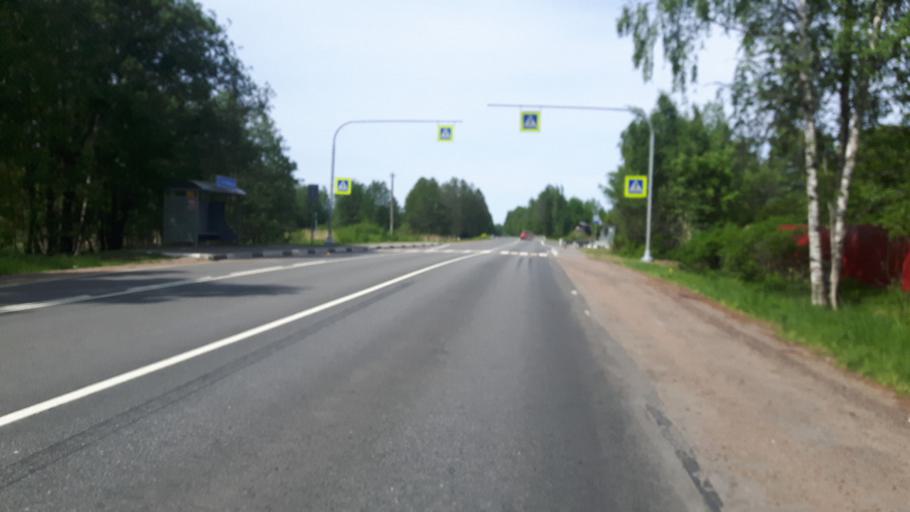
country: RU
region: Leningrad
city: Ust'-Luga
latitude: 59.6511
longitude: 28.3598
